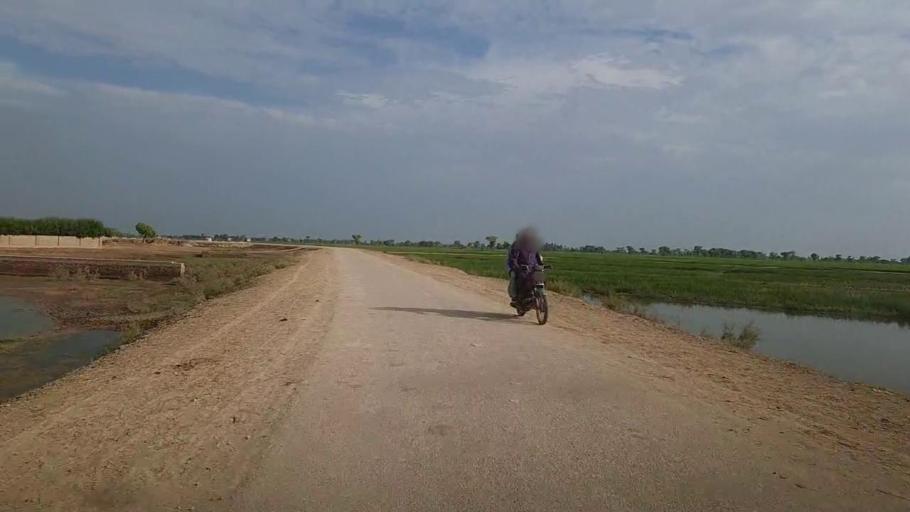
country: PK
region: Sindh
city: Thul
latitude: 28.2668
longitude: 68.8509
